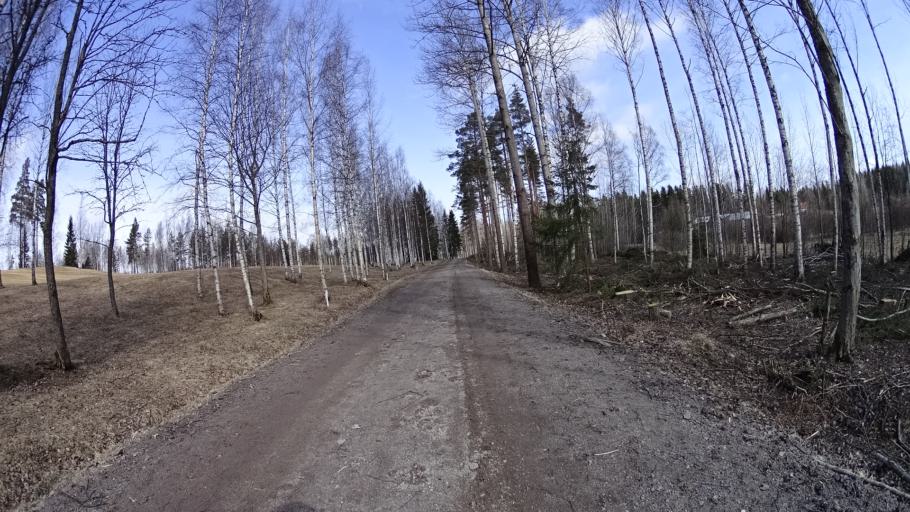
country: FI
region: Uusimaa
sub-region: Helsinki
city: Kilo
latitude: 60.3224
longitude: 24.8172
